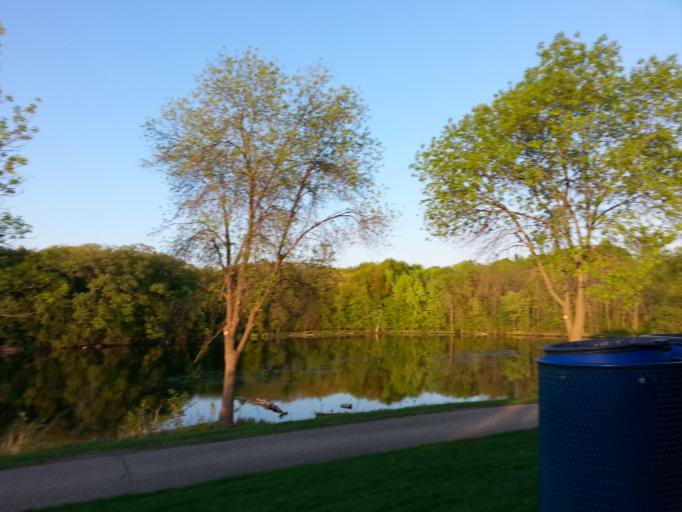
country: US
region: Minnesota
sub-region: Scott County
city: Prior Lake
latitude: 44.7214
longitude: -93.4229
